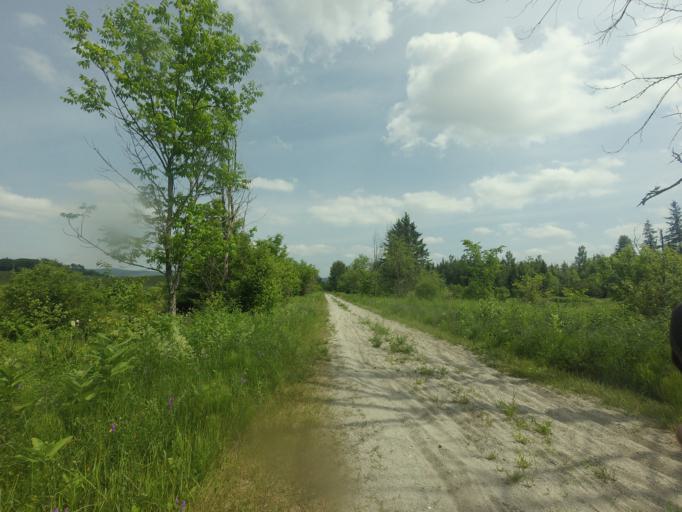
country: CA
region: Quebec
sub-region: Outaouais
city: Wakefield
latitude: 45.8145
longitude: -75.9605
